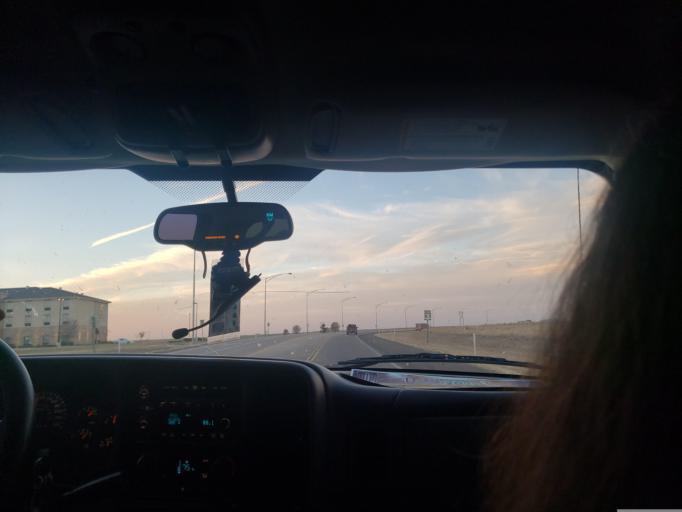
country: US
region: Kansas
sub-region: Seward County
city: Liberal
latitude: 37.0719
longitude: -100.9199
